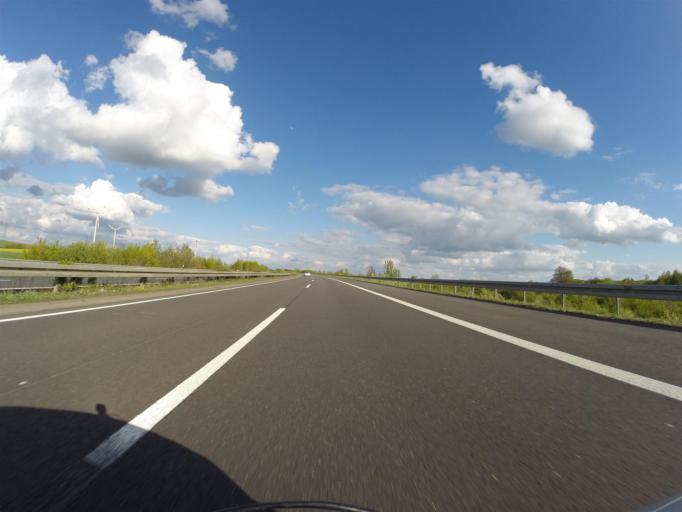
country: DE
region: Saarland
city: Orscholz
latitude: 49.4543
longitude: 6.4839
